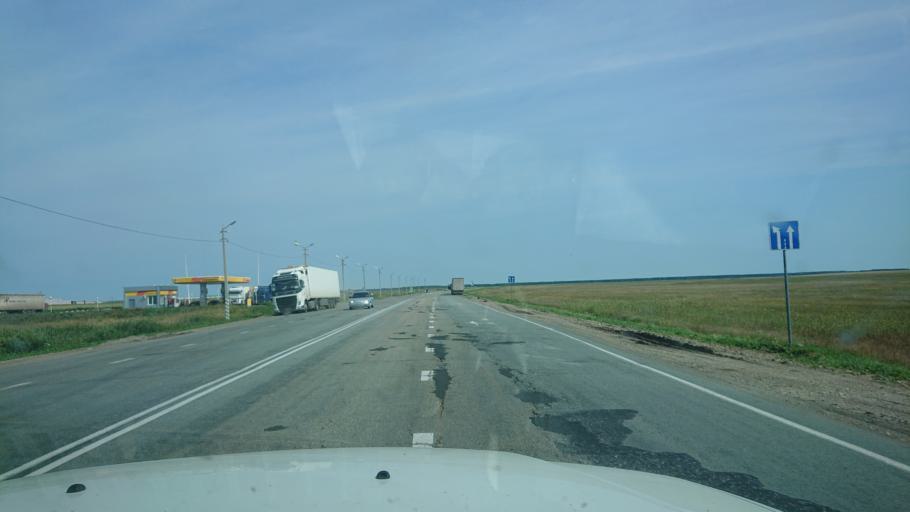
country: RU
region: Tjumen
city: Armizonskoye
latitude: 55.5354
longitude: 67.8931
